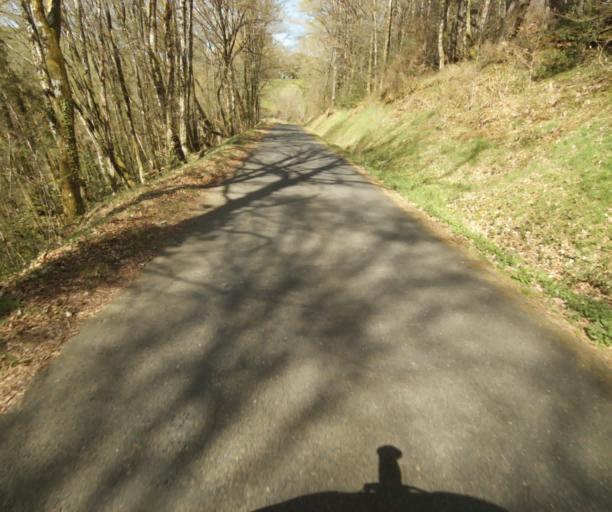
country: FR
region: Limousin
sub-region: Departement de la Correze
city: Naves
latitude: 45.3488
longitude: 1.7803
